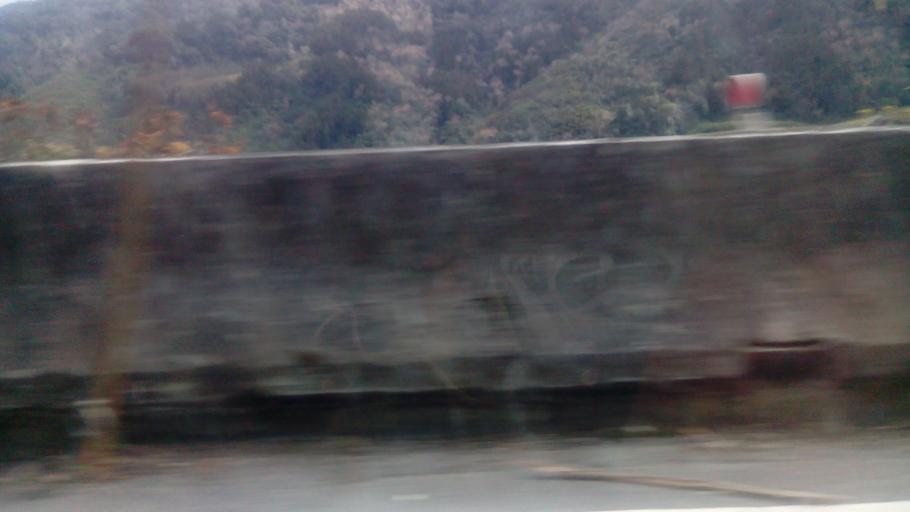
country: TW
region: Taiwan
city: Daxi
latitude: 24.4558
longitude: 121.3932
